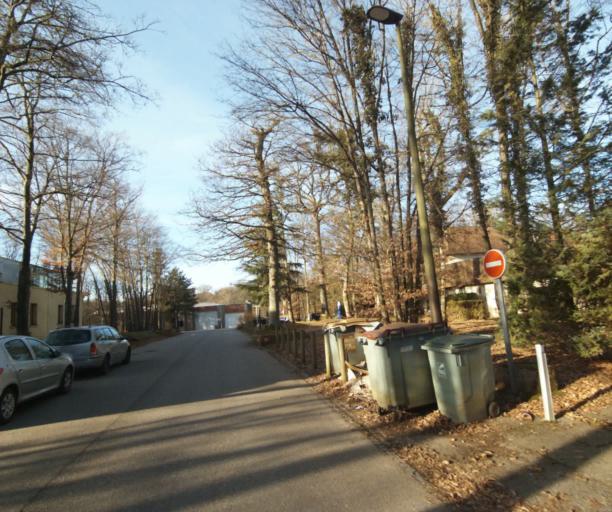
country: FR
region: Lorraine
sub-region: Departement de Meurthe-et-Moselle
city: Chavigny
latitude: 48.6516
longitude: 6.1353
